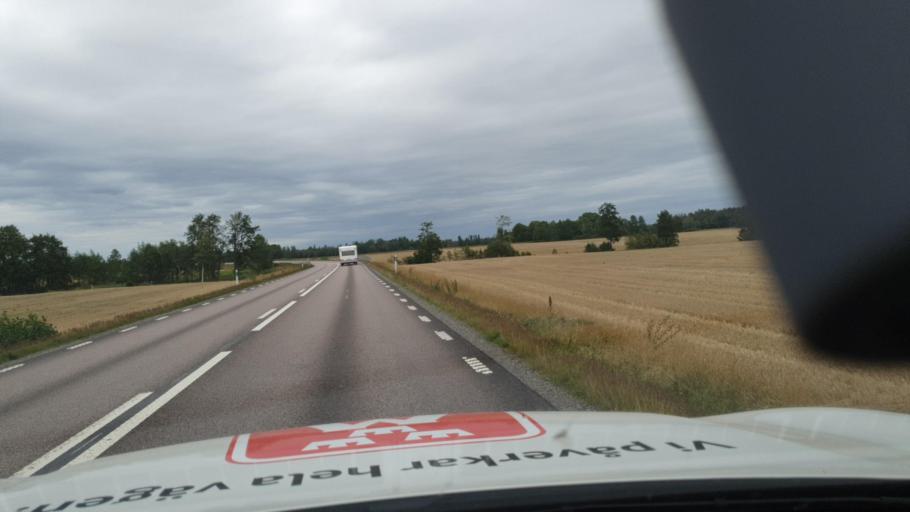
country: SE
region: Vaestra Goetaland
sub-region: Melleruds Kommun
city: Mellerud
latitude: 58.6450
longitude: 12.4143
